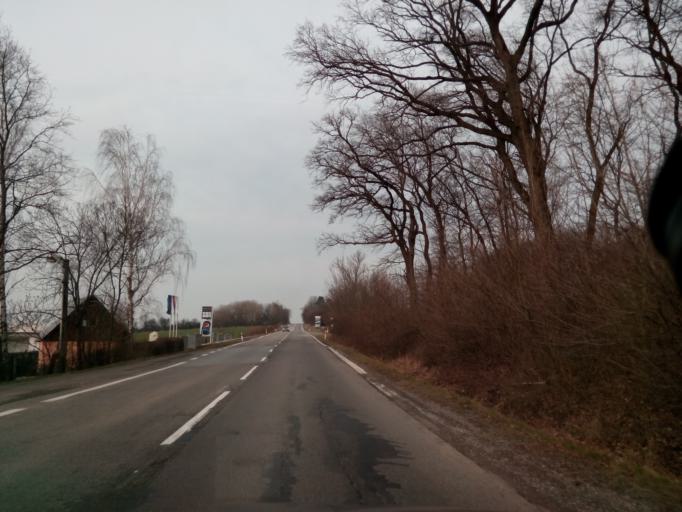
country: HU
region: Borsod-Abauj-Zemplen
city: Satoraljaujhely
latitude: 48.5042
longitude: 21.6539
